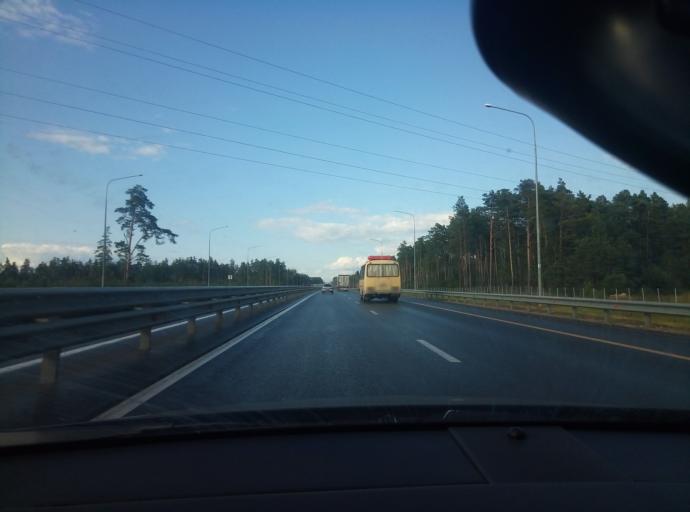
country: RU
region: Kaluga
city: Kurovskoye
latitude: 54.5746
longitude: 36.0603
